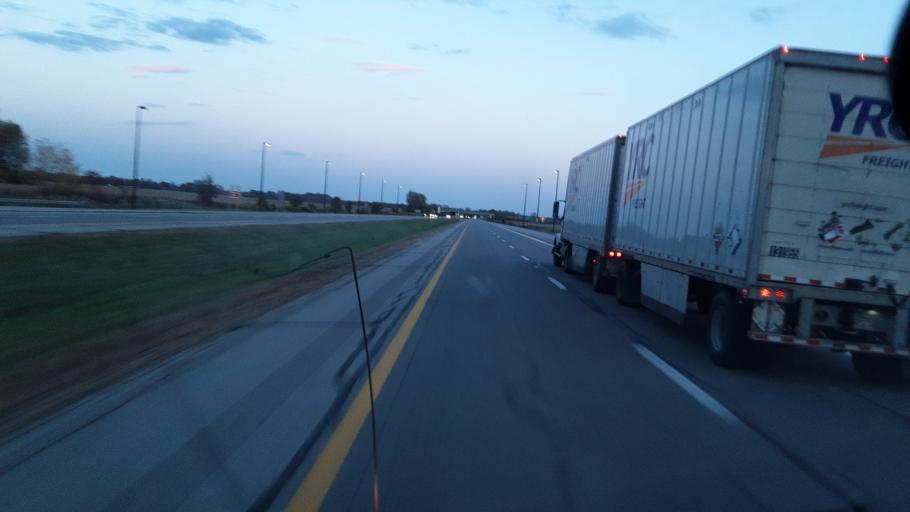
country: US
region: Ohio
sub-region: Williams County
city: West Unity
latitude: 41.6043
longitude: -84.4061
